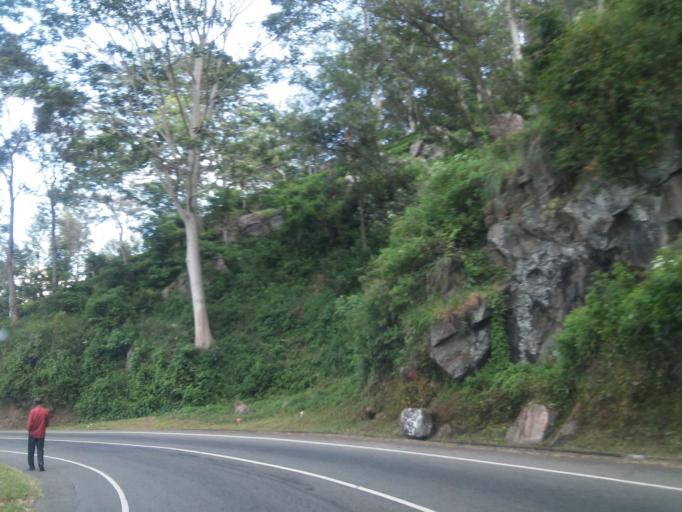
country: LK
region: Uva
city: Haputale
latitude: 6.7635
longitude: 80.9202
